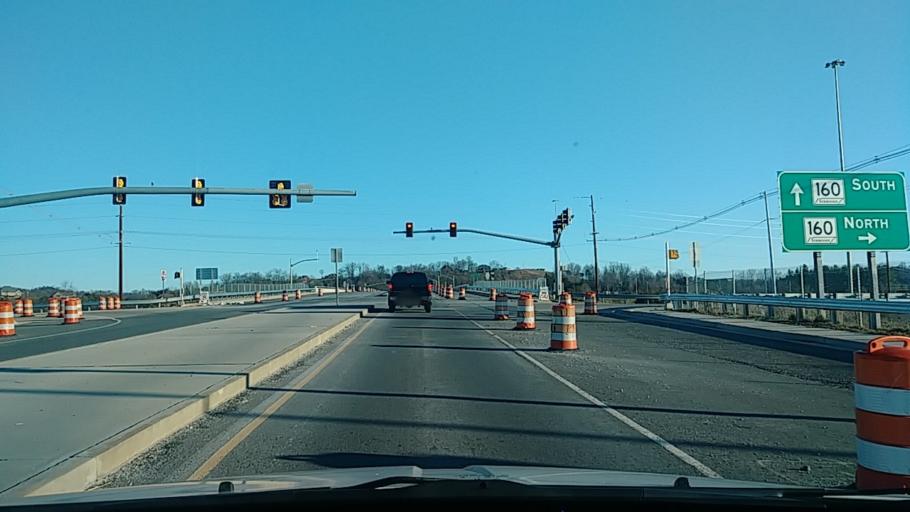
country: US
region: Tennessee
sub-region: Hamblen County
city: Morristown
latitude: 36.1769
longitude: -83.3482
